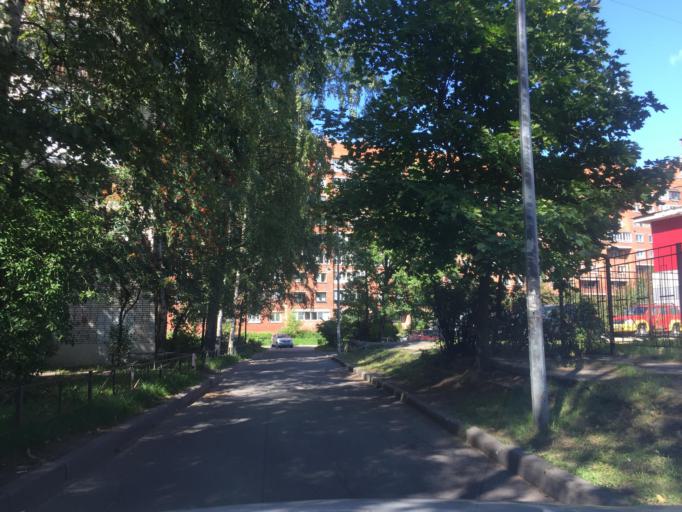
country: RU
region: Leningrad
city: Akademicheskoe
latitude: 60.0077
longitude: 30.4072
